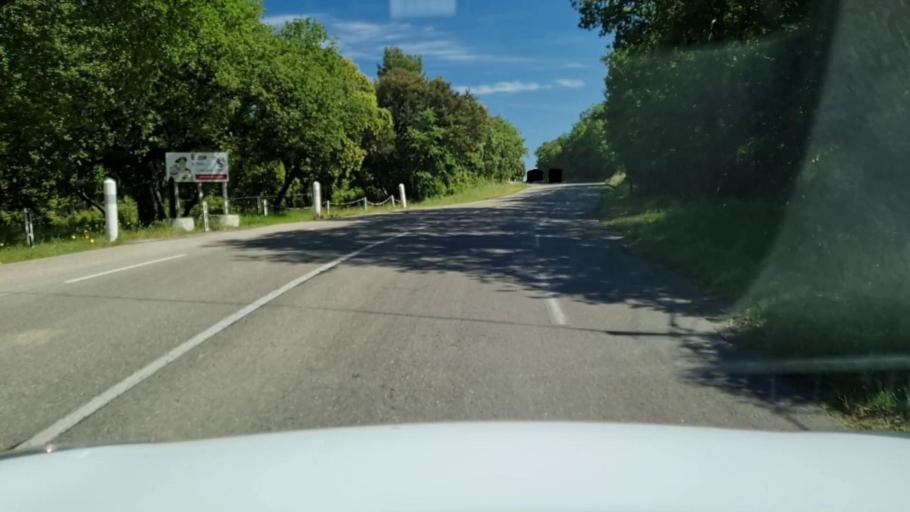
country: FR
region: Languedoc-Roussillon
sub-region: Departement du Gard
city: Sommieres
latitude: 43.8012
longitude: 4.0863
